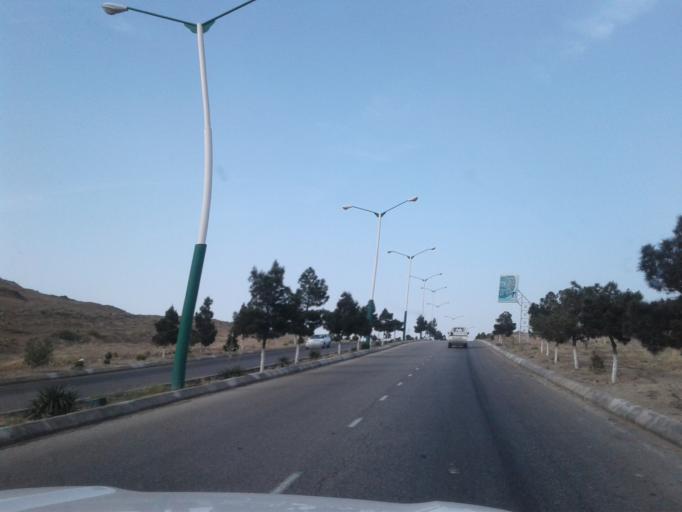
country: TM
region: Balkan
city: Turkmenbasy
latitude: 40.0103
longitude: 52.9459
